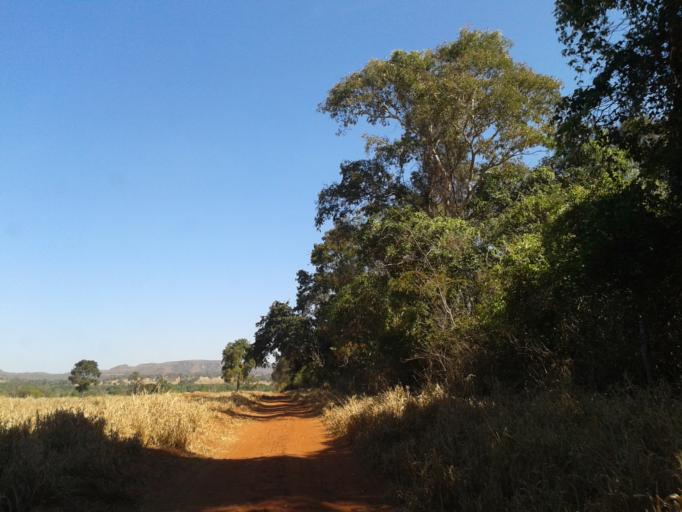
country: BR
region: Minas Gerais
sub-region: Santa Vitoria
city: Santa Vitoria
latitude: -19.1379
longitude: -50.0392
